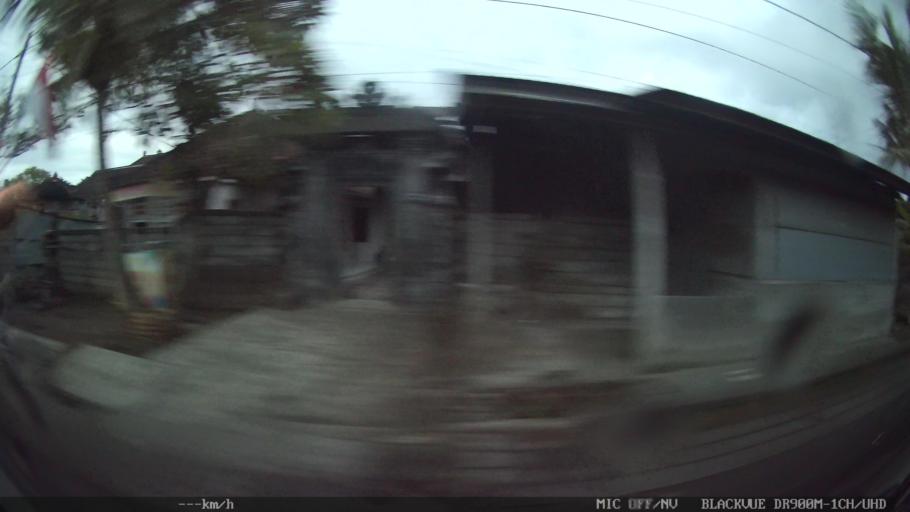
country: ID
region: Bali
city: Banjar Pasekan
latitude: -8.6205
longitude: 115.2729
